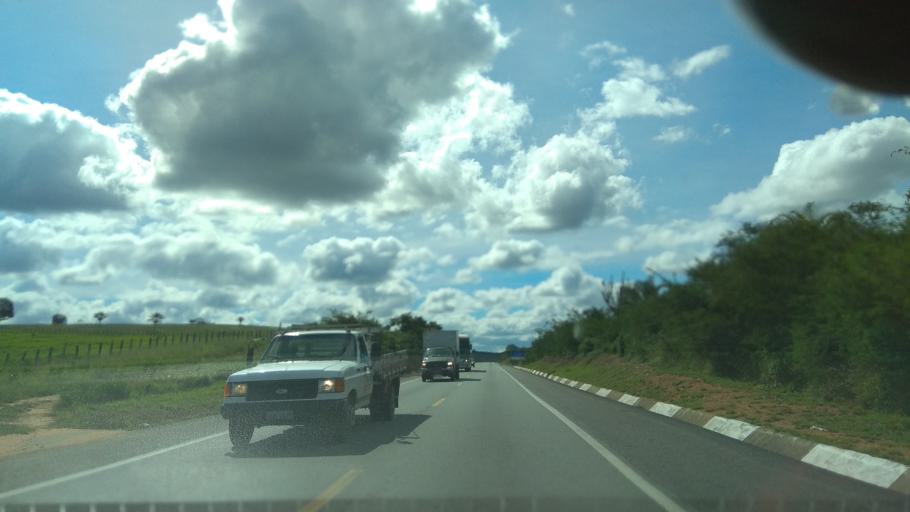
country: BR
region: Bahia
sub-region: Santa Ines
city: Santa Ines
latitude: -13.3204
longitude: -40.0170
